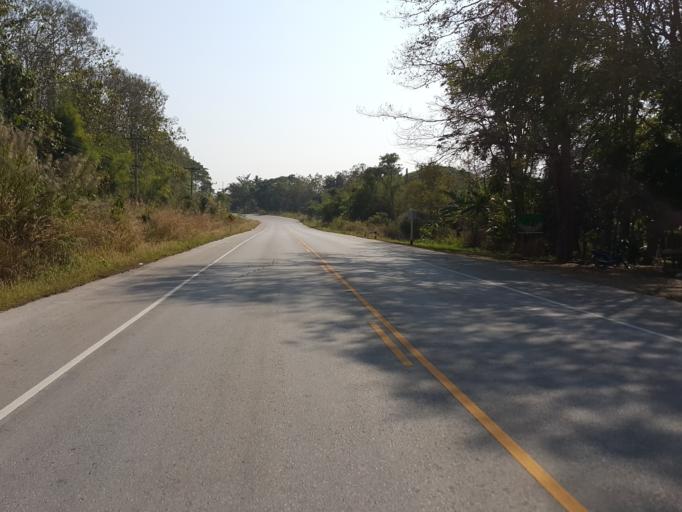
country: TH
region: Lampang
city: Mueang Pan
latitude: 18.8024
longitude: 99.5872
